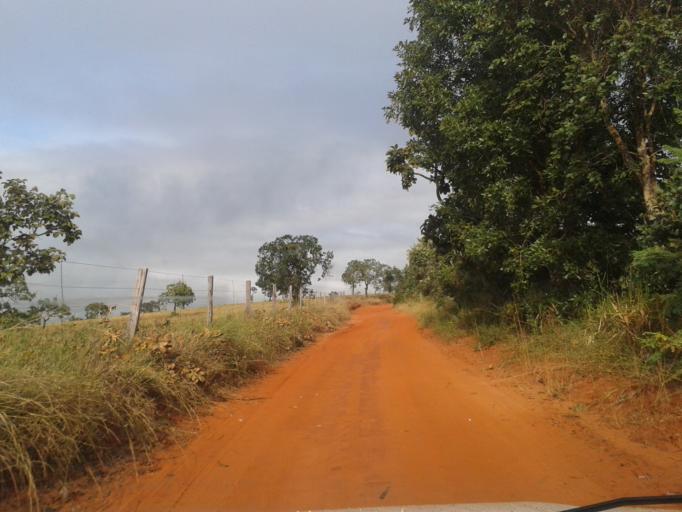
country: BR
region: Minas Gerais
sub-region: Campina Verde
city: Campina Verde
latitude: -19.4000
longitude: -49.6206
